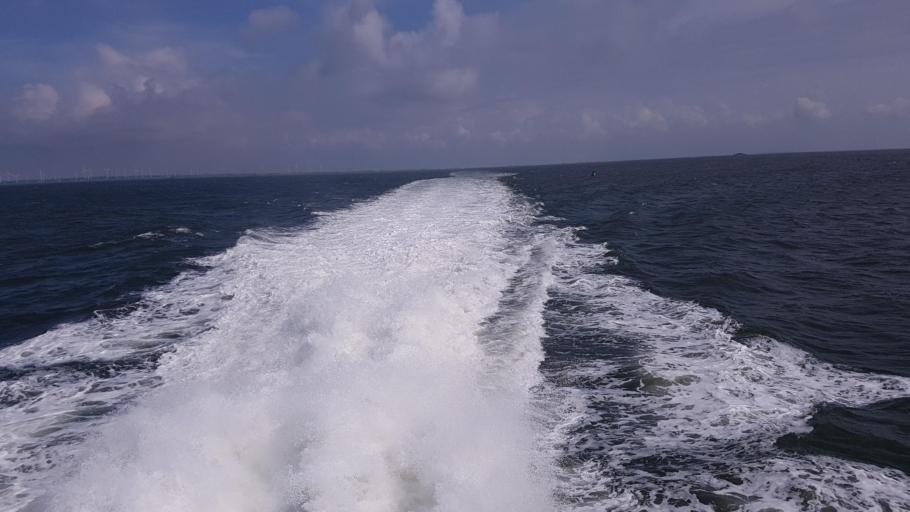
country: DE
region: Schleswig-Holstein
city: Grode
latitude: 54.6210
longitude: 8.7651
